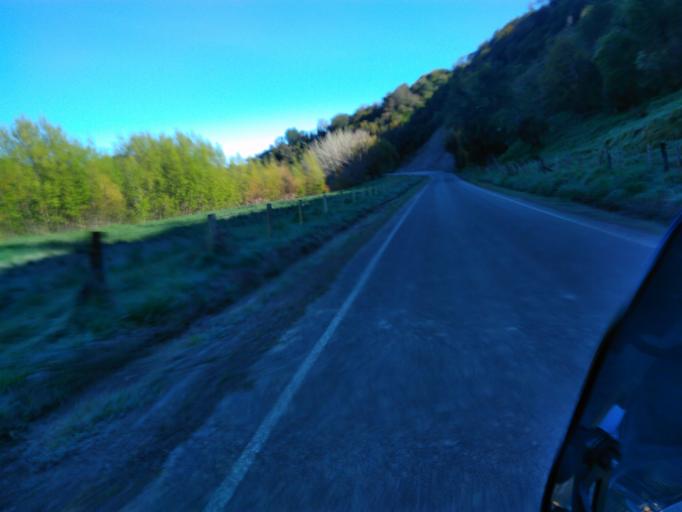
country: NZ
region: Gisborne
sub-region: Gisborne District
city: Gisborne
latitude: -38.4531
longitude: 177.7689
